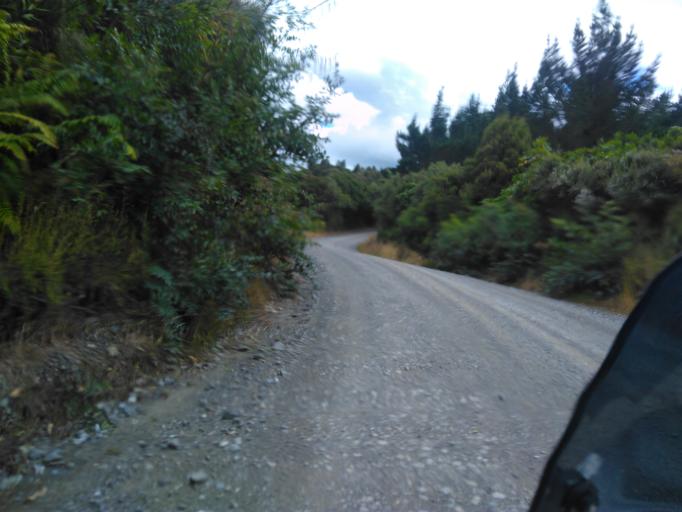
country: NZ
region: Gisborne
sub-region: Gisborne District
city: Gisborne
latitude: -38.1656
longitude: 178.1366
